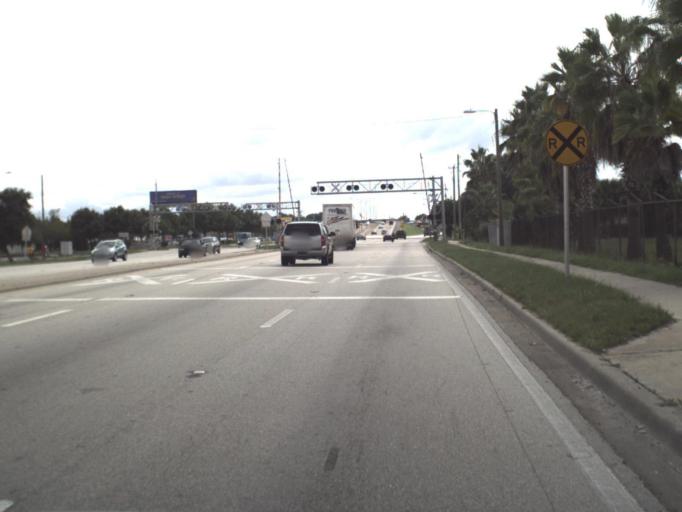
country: US
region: Florida
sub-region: Manatee County
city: Bradenton
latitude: 27.4877
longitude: -82.5630
